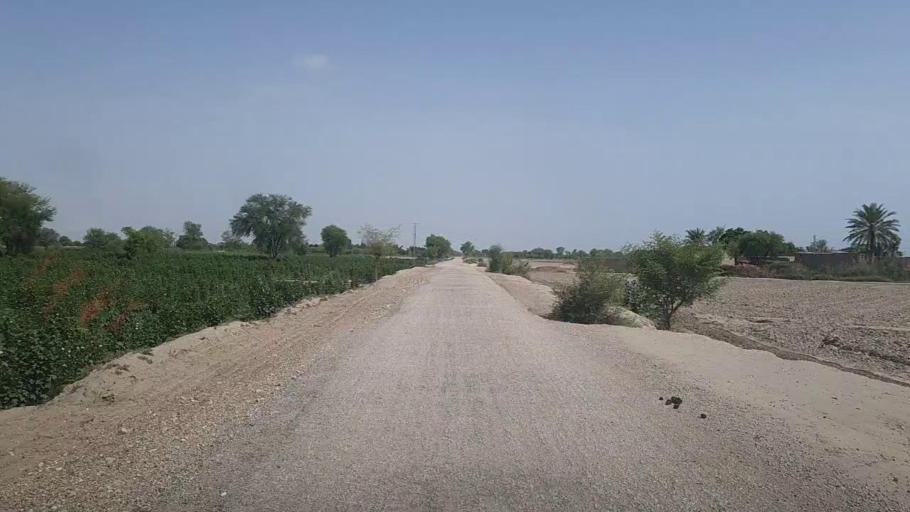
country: PK
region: Sindh
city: Pad Idan
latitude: 26.7584
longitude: 68.3397
